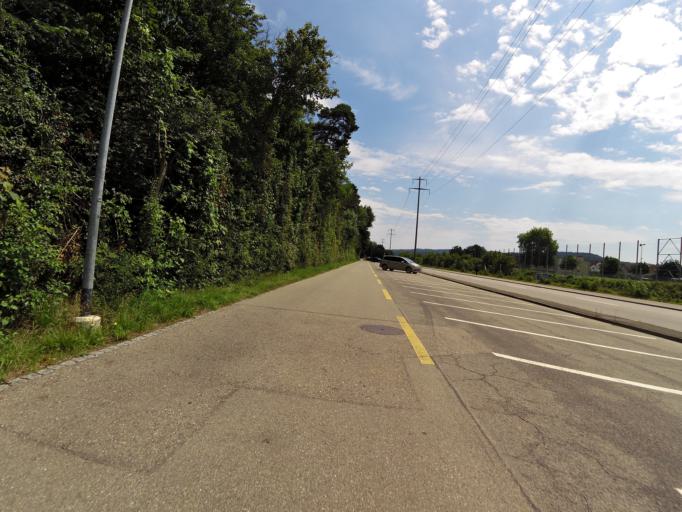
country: CH
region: Thurgau
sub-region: Frauenfeld District
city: Frauenfeld
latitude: 47.5659
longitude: 8.8879
